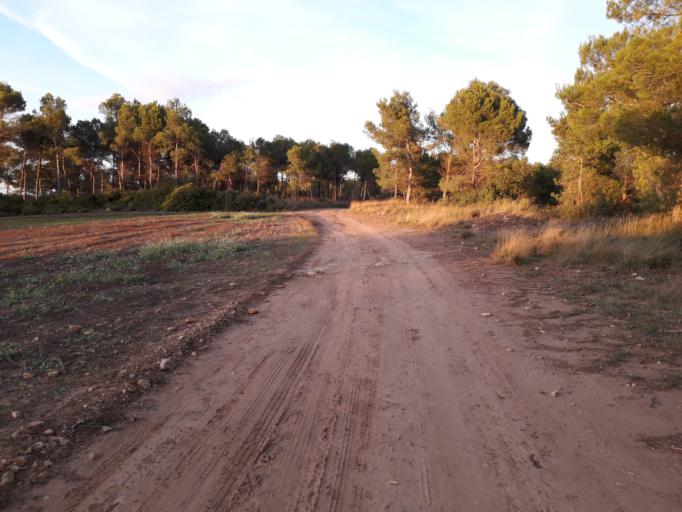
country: ES
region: Catalonia
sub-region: Provincia de Barcelona
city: Jorba
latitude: 41.6125
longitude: 1.5625
